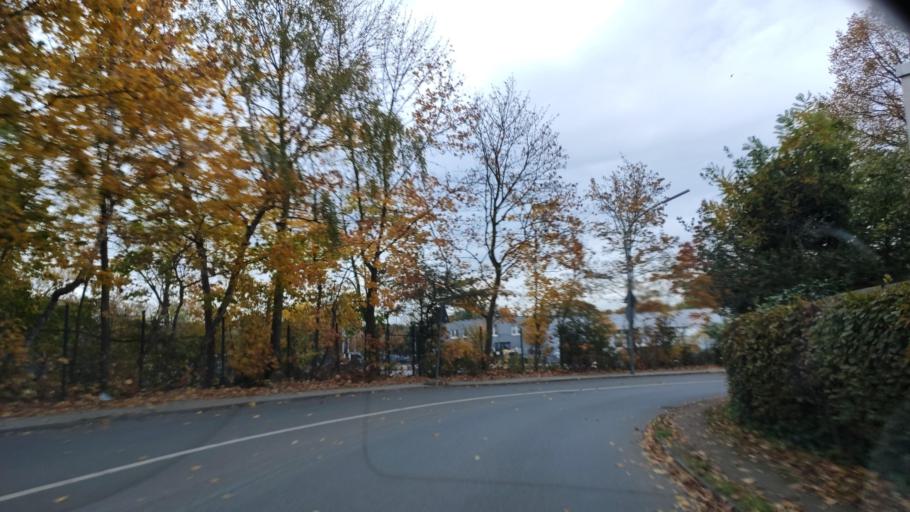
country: DE
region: North Rhine-Westphalia
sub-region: Regierungsbezirk Munster
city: Gelsenkirchen
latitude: 51.5474
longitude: 7.0715
